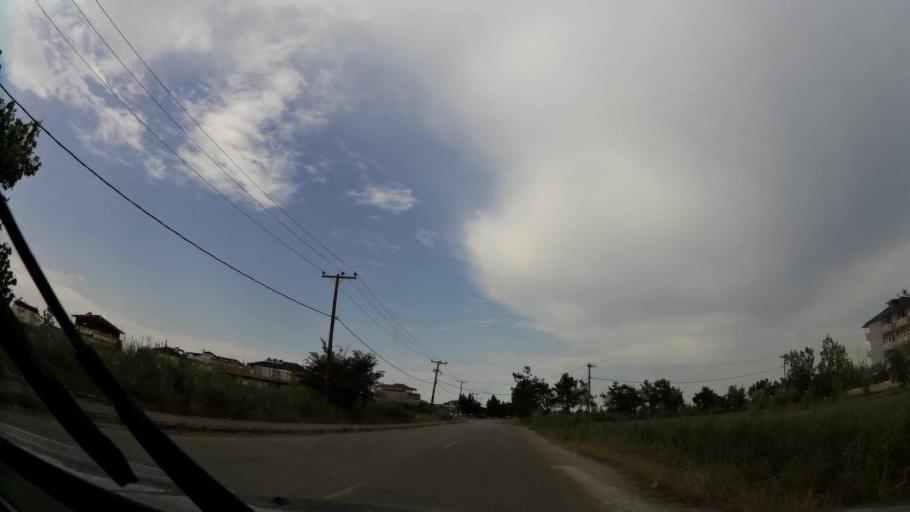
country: GR
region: Central Macedonia
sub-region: Nomos Pierias
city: Paralia
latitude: 40.2731
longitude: 22.5955
